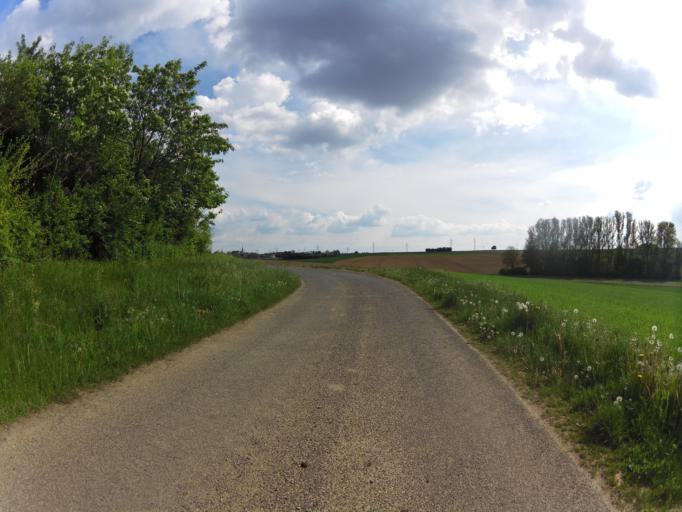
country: DE
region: Bavaria
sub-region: Regierungsbezirk Unterfranken
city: Giebelstadt
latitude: 49.6181
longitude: 9.9423
